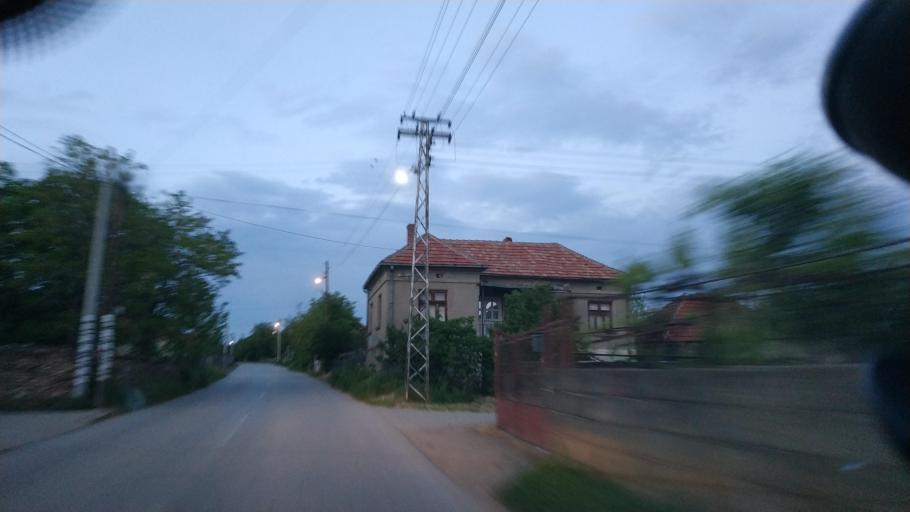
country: RS
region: Central Serbia
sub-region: Nisavski Okrug
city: Merosina
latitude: 43.2970
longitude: 21.7048
